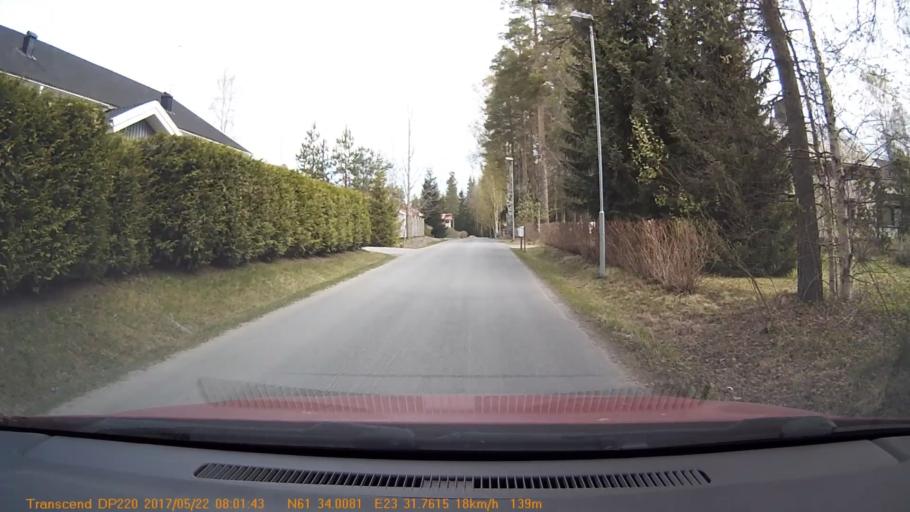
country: FI
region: Pirkanmaa
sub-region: Tampere
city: Yloejaervi
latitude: 61.5669
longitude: 23.5294
